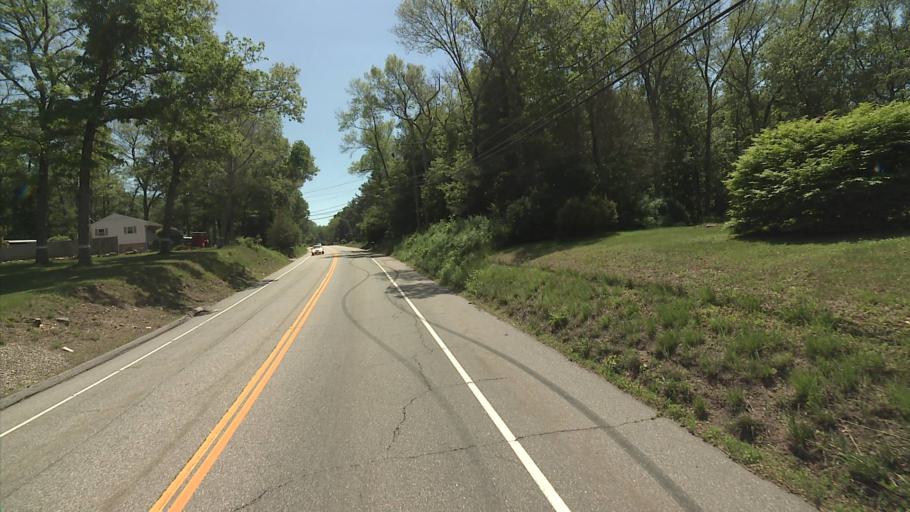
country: US
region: Connecticut
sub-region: Tolland County
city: Tolland
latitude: 41.8933
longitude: -72.3986
